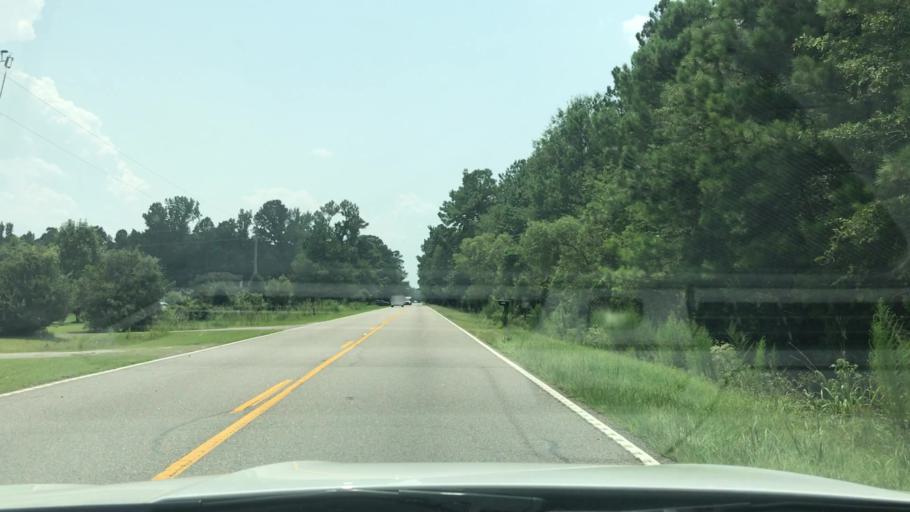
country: US
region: South Carolina
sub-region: Georgetown County
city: Georgetown
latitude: 33.5347
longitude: -79.2346
